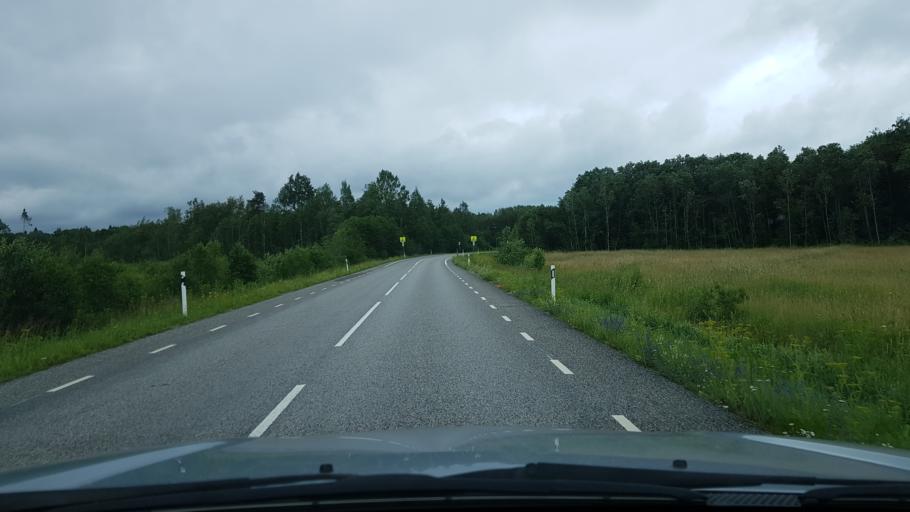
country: EE
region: Ida-Virumaa
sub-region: Narva-Joesuu linn
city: Narva-Joesuu
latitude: 59.3662
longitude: 27.9310
